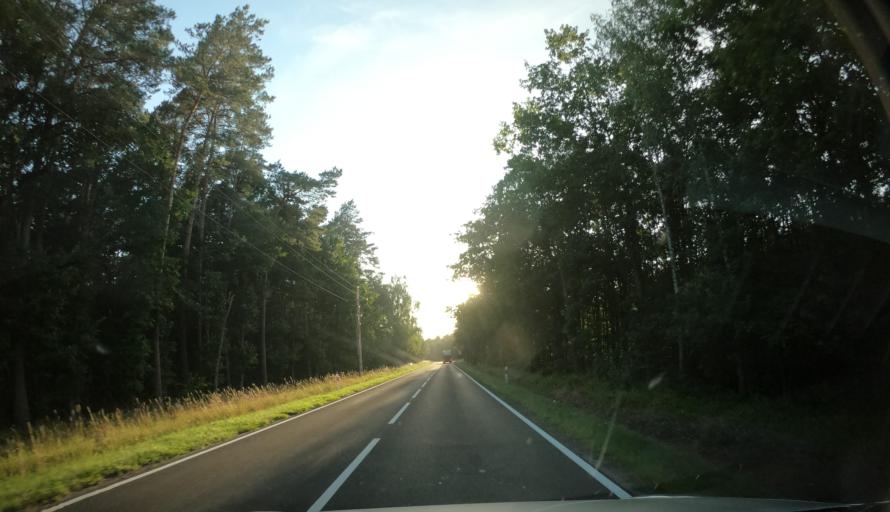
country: PL
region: Kujawsko-Pomorskie
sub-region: Powiat bydgoski
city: Koronowo
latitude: 53.3111
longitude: 18.0308
